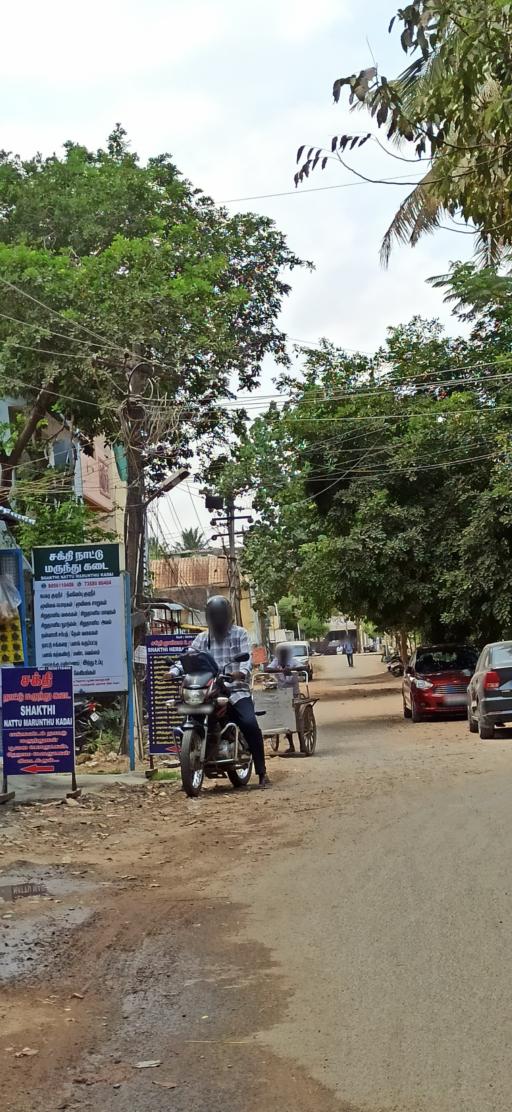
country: IN
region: Tamil Nadu
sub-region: Thiruvallur
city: Porur
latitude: 13.0186
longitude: 80.1468
